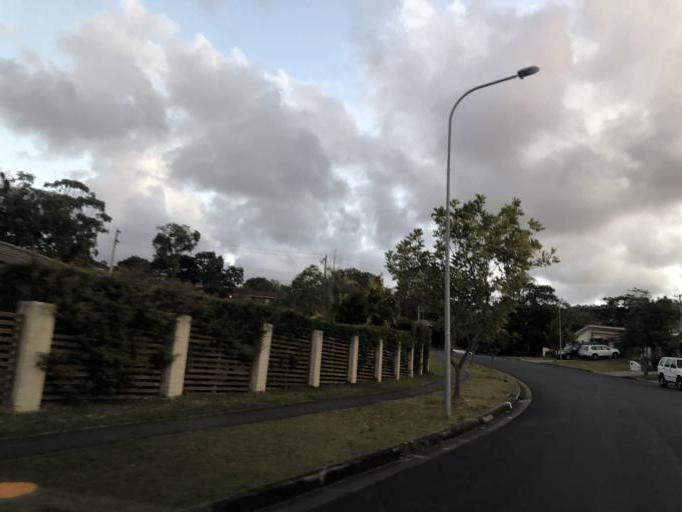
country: AU
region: New South Wales
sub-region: Coffs Harbour
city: Woolgoolga
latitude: -30.0958
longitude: 153.1919
